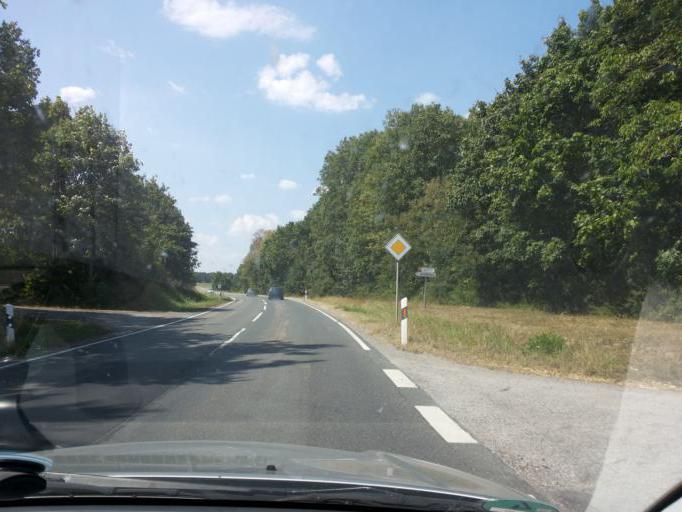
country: DE
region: Bavaria
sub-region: Regierungsbezirk Mittelfranken
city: Markt Erlbach
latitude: 49.4972
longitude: 10.6450
